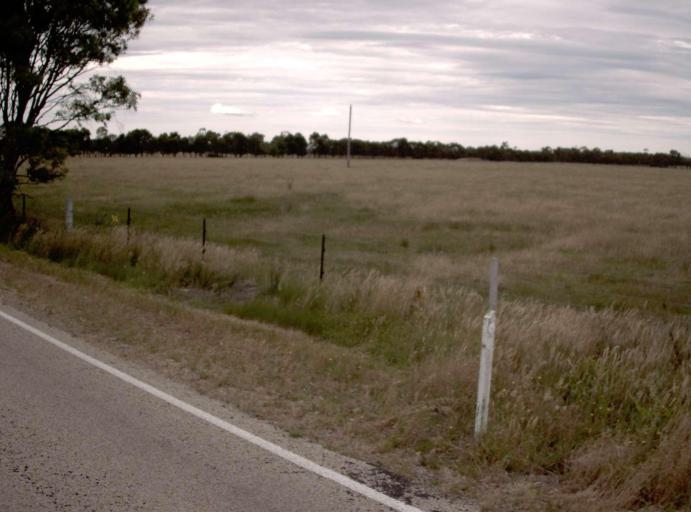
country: AU
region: Victoria
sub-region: East Gippsland
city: Bairnsdale
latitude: -37.9295
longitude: 147.5395
